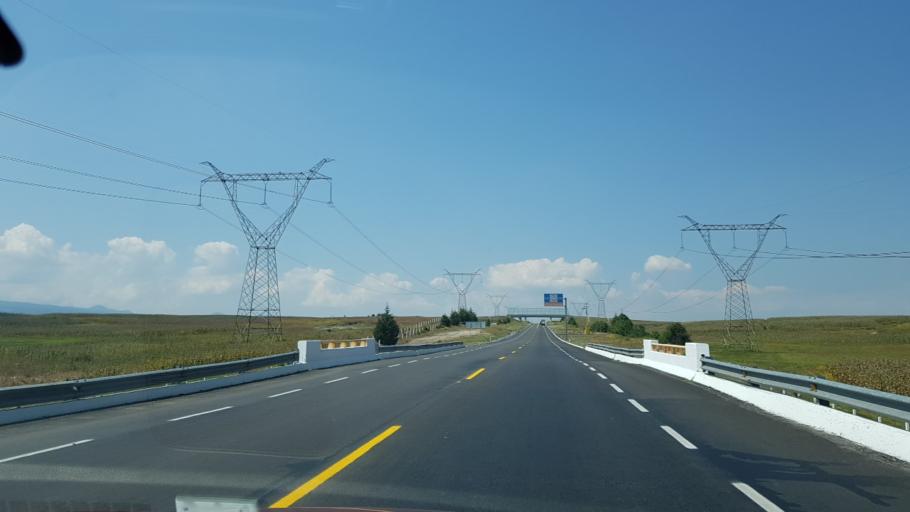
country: MX
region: Mexico
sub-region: Almoloya de Juarez
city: Conjunto Habitacional Ecologico SUTEYM
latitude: 19.3840
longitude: -99.7759
